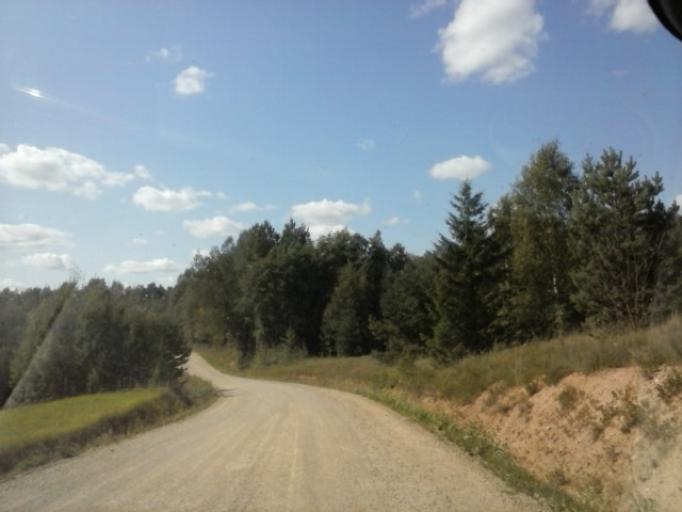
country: EE
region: Polvamaa
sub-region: Polva linn
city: Polva
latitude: 58.0994
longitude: 26.8418
